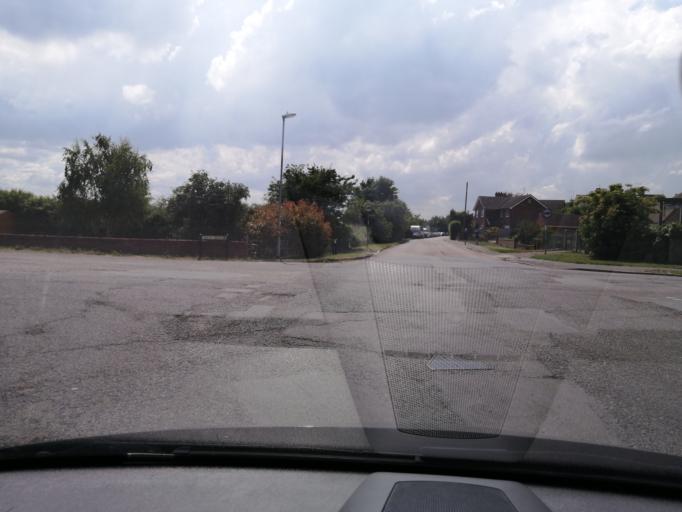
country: GB
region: England
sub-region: Cambridgeshire
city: Yaxley
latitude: 52.5159
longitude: -0.2471
